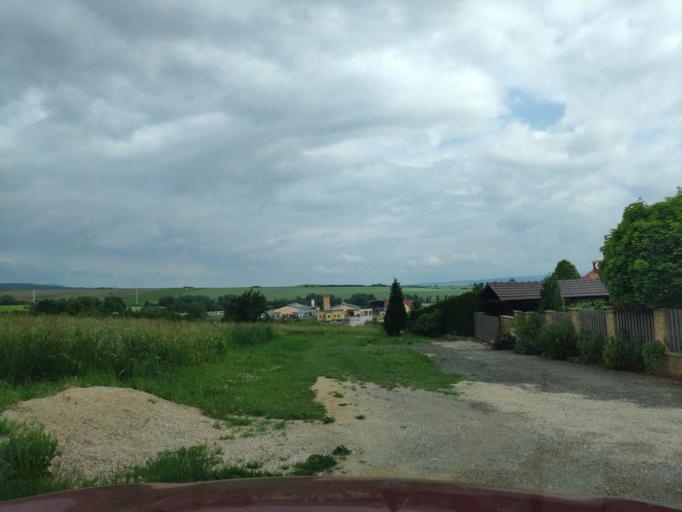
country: SK
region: Kosicky
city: Kosice
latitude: 48.8038
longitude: 21.2982
